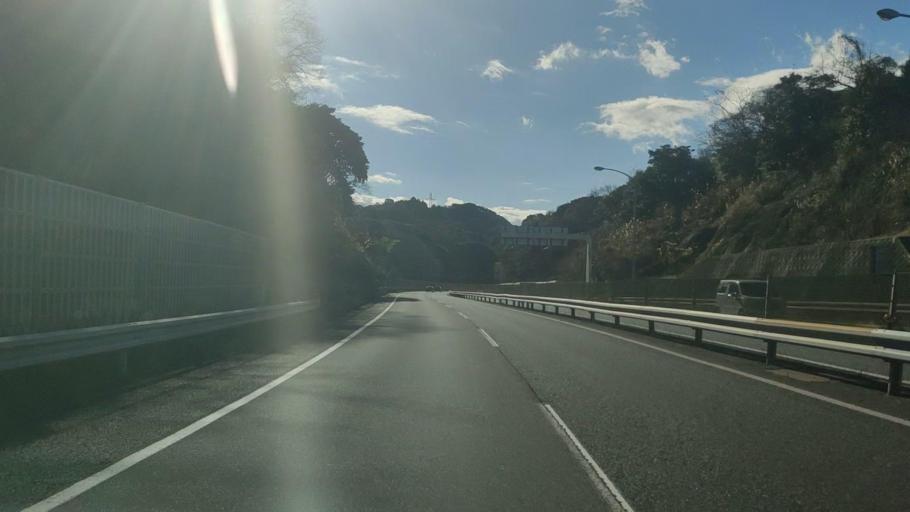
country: JP
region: Fukuoka
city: Kitakyushu
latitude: 33.8570
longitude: 130.8432
